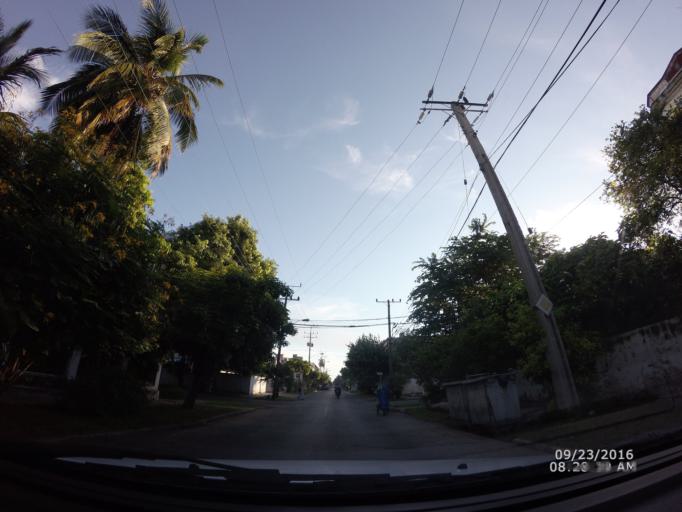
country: CU
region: La Habana
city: Havana
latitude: 23.1344
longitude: -82.3926
